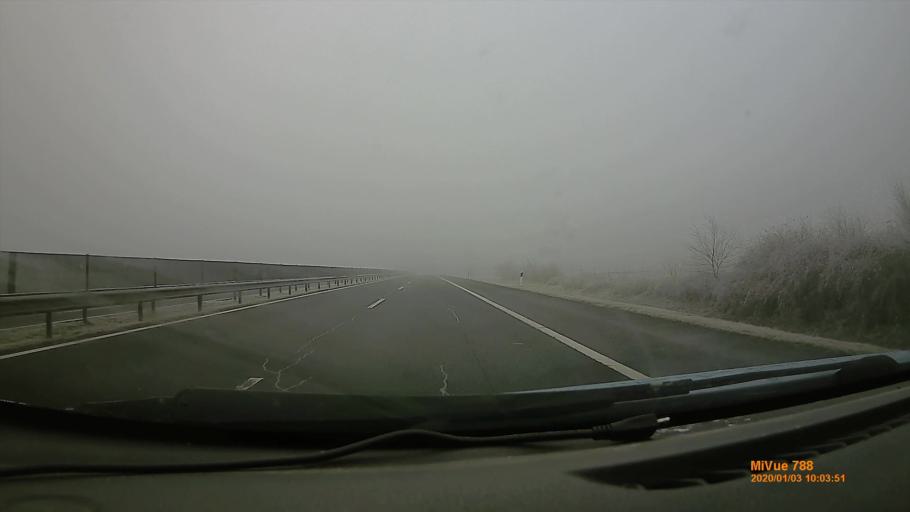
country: HU
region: Fejer
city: Eloszallas
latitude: 46.7990
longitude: 18.8621
